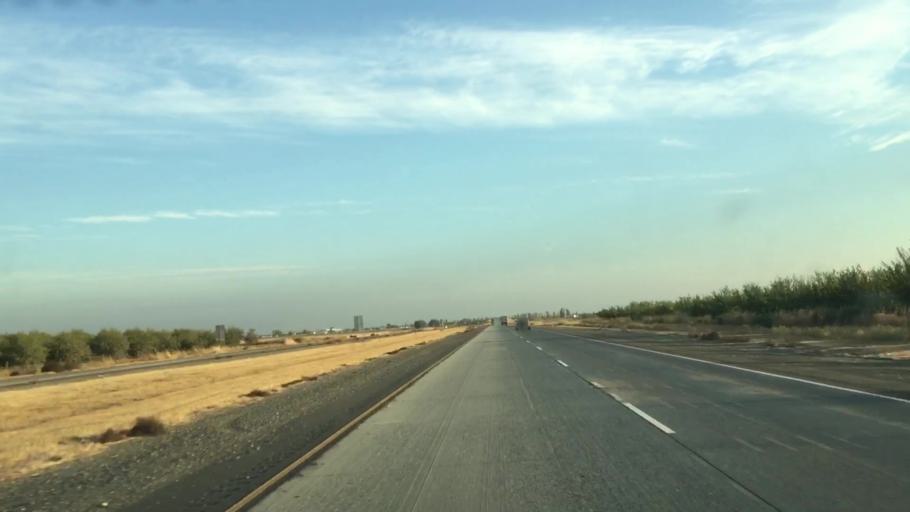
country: US
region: California
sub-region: Yolo County
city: Dunnigan
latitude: 38.8360
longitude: -121.9394
